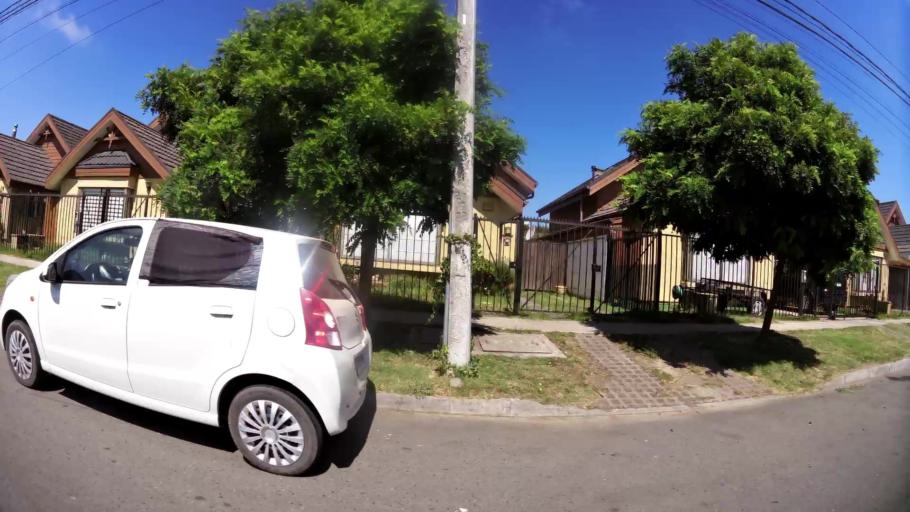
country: CL
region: Biobio
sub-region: Provincia de Concepcion
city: Concepcion
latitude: -36.7775
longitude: -73.0458
